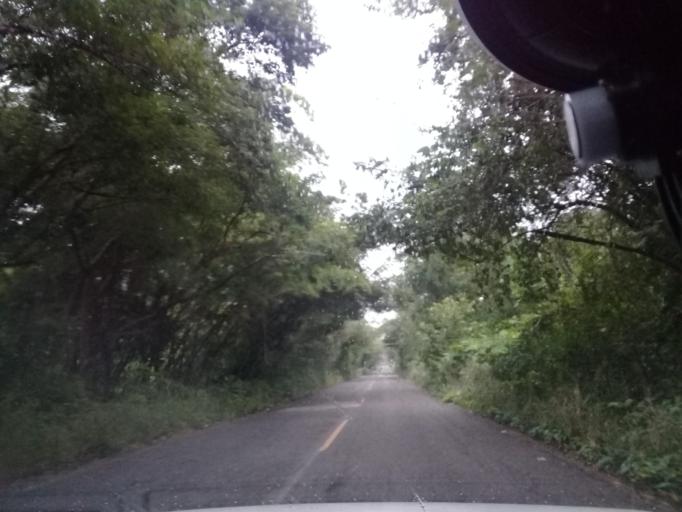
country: MX
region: Veracruz
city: Platon Sanchez
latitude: 21.2256
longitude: -98.3771
